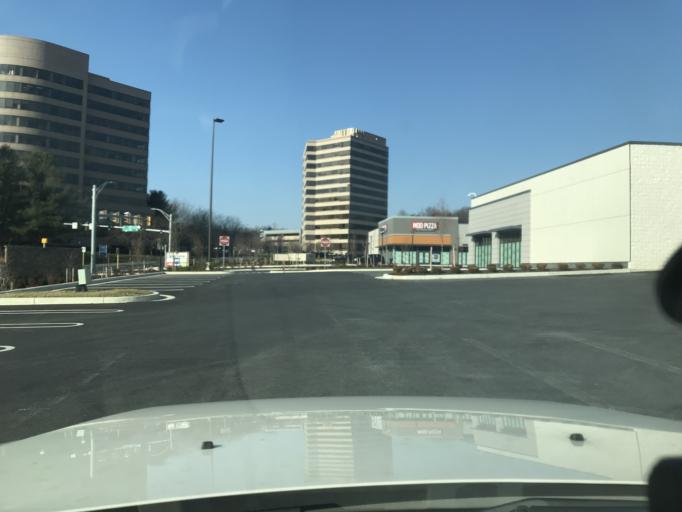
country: US
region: Maryland
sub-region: Baltimore County
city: Owings Mills
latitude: 39.4054
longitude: -76.7919
